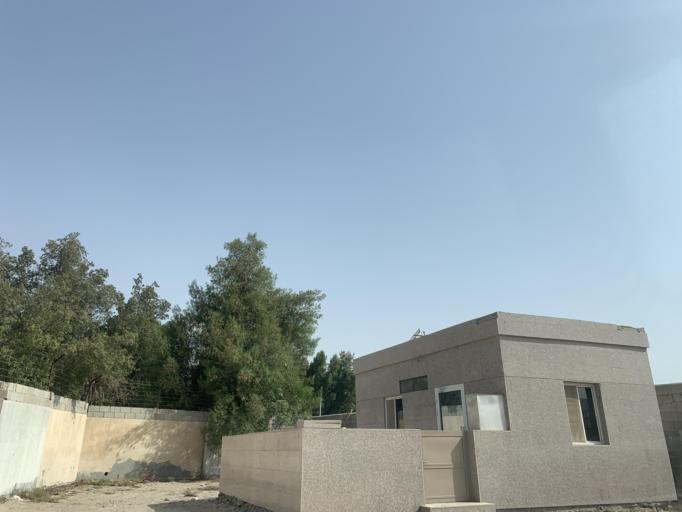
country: BH
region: Manama
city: Jidd Hafs
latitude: 26.2142
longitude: 50.5102
